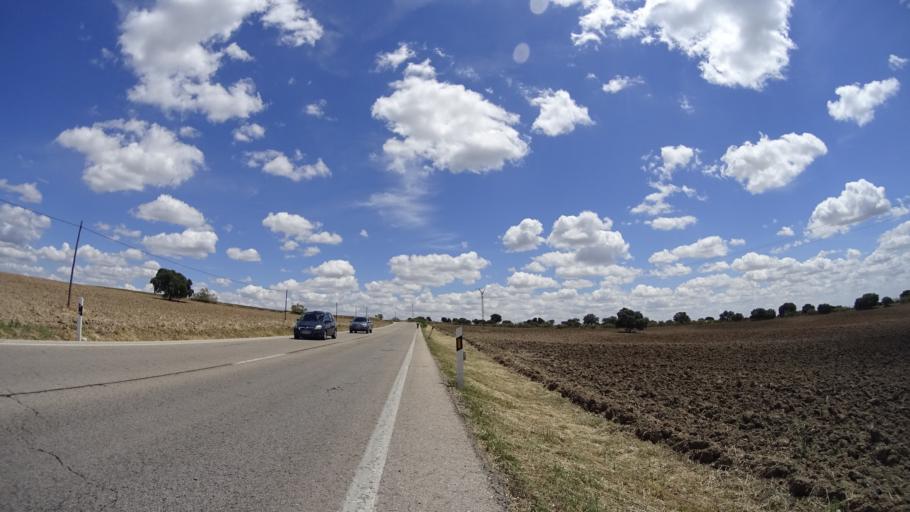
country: ES
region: Madrid
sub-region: Provincia de Madrid
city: Boadilla del Monte
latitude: 40.4136
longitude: -3.9344
